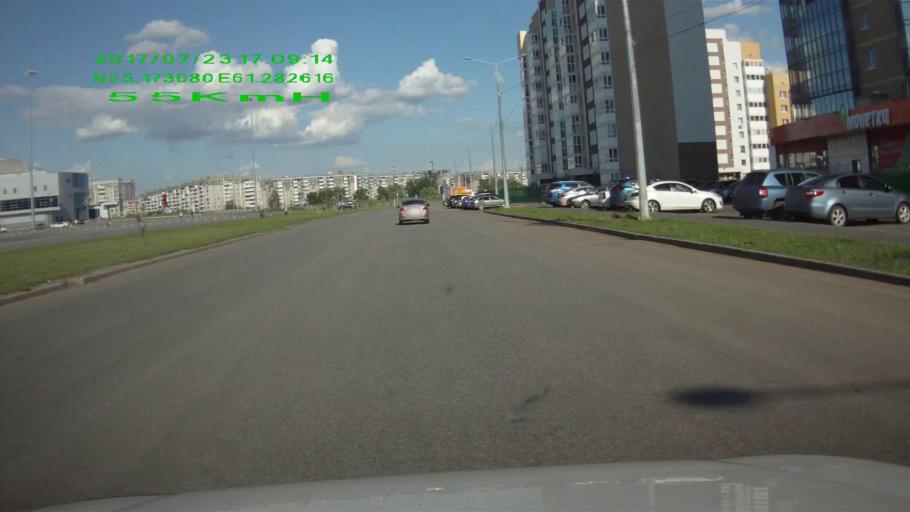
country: RU
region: Chelyabinsk
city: Roshchino
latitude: 55.1721
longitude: 61.2812
